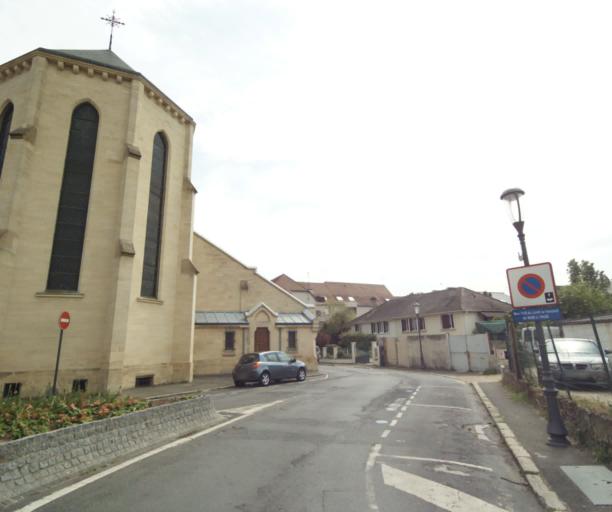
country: FR
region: Ile-de-France
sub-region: Departement des Yvelines
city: Les Mureaux
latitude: 48.9926
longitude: 1.9071
